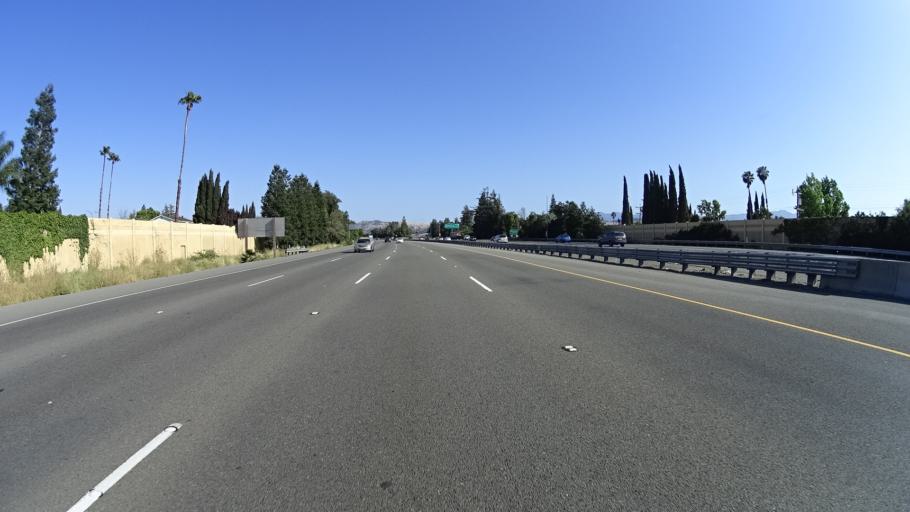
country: US
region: California
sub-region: Santa Clara County
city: Seven Trees
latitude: 37.2634
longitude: -121.8008
